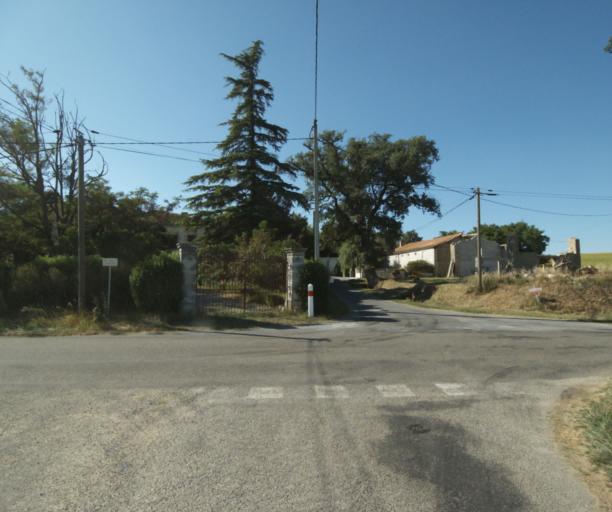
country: FR
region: Midi-Pyrenees
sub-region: Departement de la Haute-Garonne
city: Saint-Felix-Lauragais
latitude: 43.4943
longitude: 1.9411
